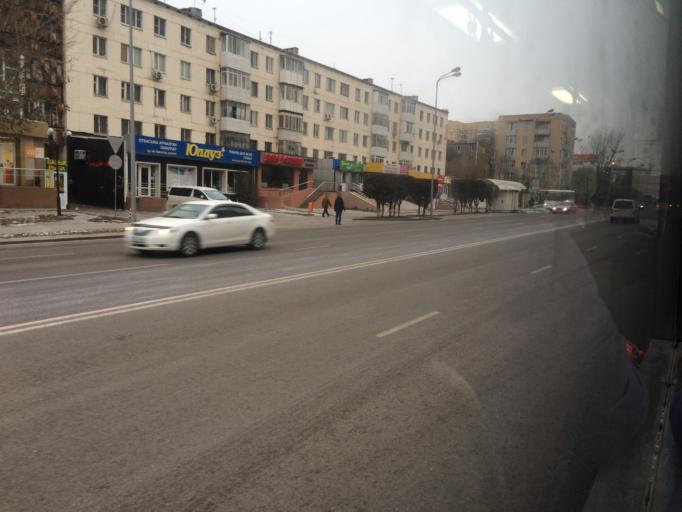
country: KZ
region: Astana Qalasy
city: Astana
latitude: 51.1677
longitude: 71.4399
